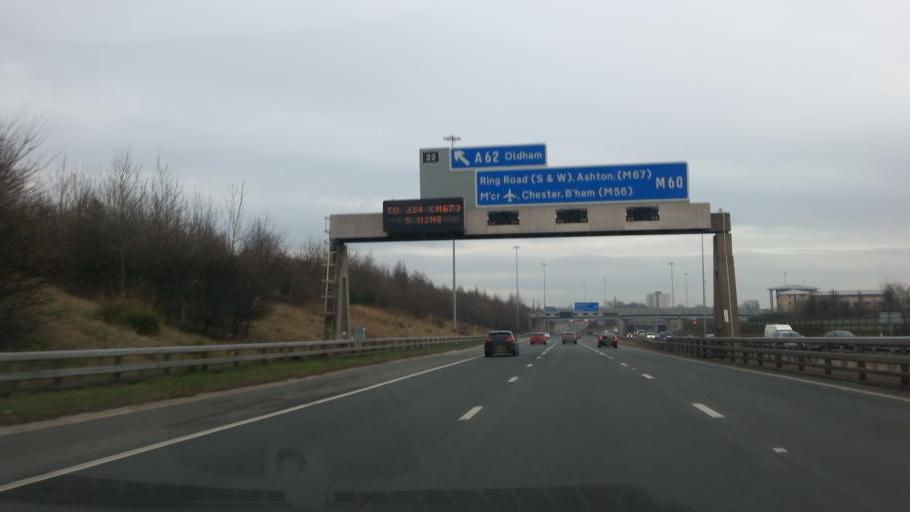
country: GB
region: England
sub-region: Manchester
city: Failsworth
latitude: 53.5224
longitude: -2.1510
